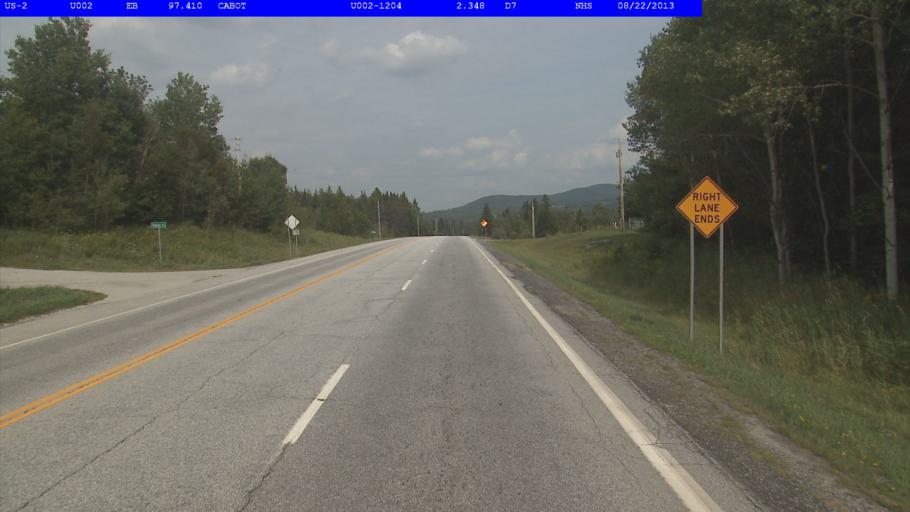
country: US
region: Vermont
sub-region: Caledonia County
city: Hardwick
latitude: 44.3676
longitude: -72.2800
